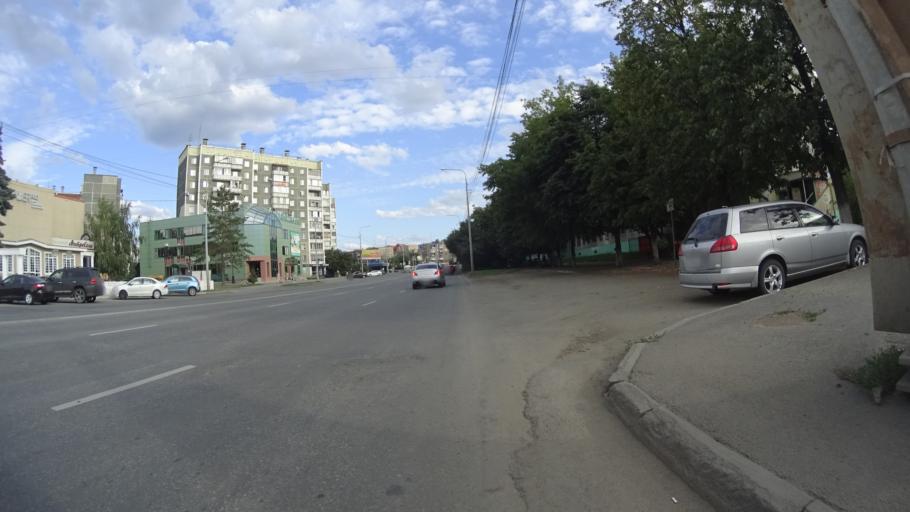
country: RU
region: Chelyabinsk
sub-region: Gorod Chelyabinsk
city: Chelyabinsk
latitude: 55.1998
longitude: 61.3299
